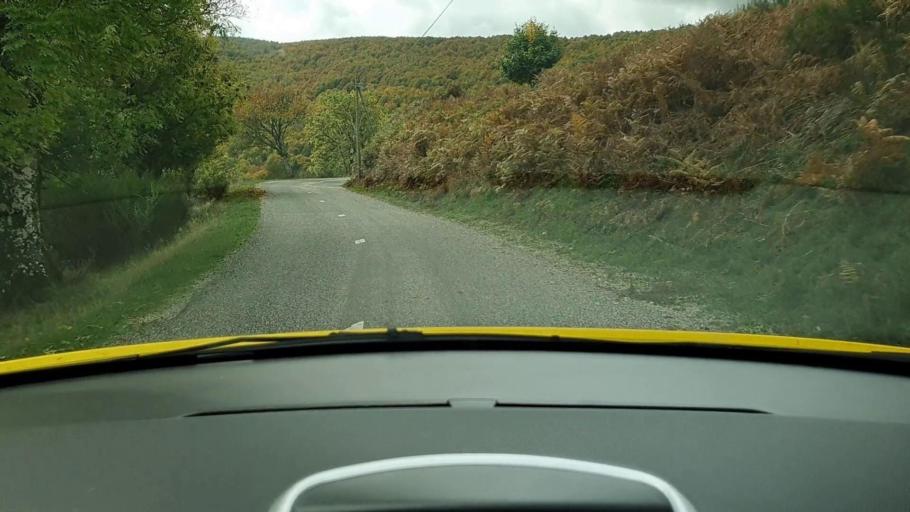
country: FR
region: Languedoc-Roussillon
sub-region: Departement du Gard
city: Le Vigan
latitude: 44.0731
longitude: 3.5179
